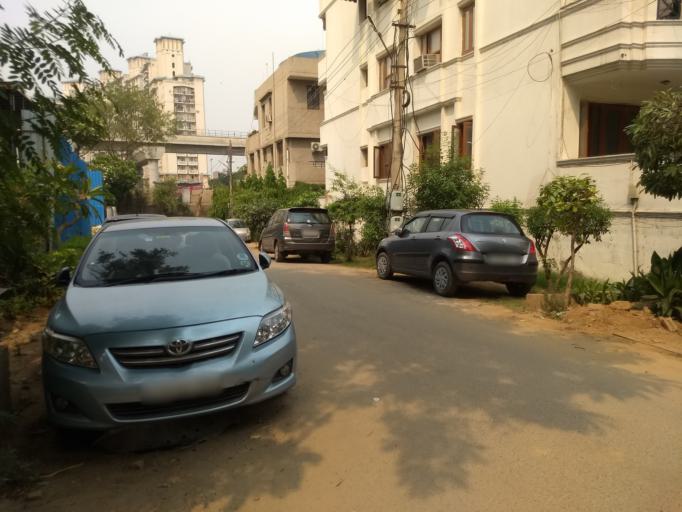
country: IN
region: Haryana
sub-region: Gurgaon
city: Gurgaon
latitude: 28.4886
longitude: 77.0893
